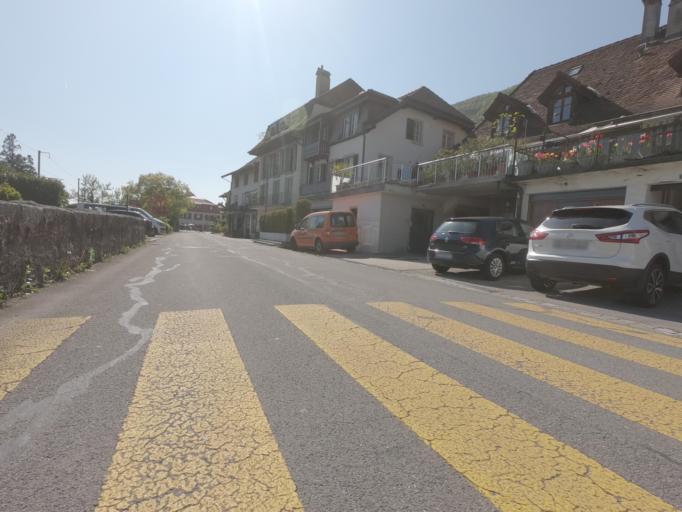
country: CH
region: Bern
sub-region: Jura bernois
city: La Neuveville
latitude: 47.0844
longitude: 7.1363
